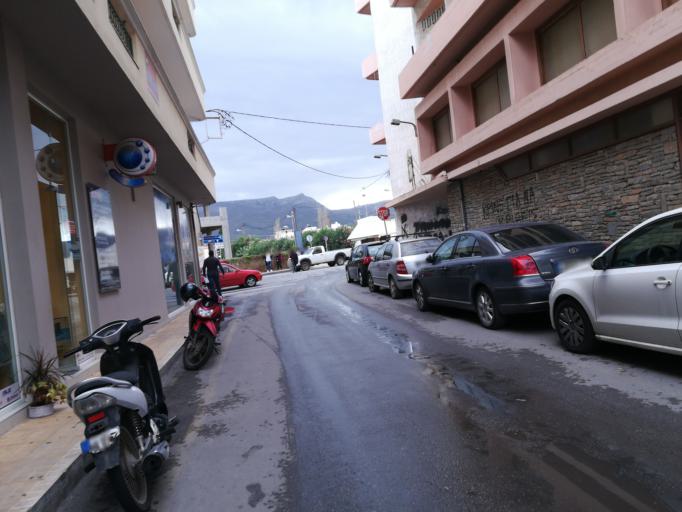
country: GR
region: Crete
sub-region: Nomos Lasithiou
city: Siteia
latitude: 35.2066
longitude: 26.1063
